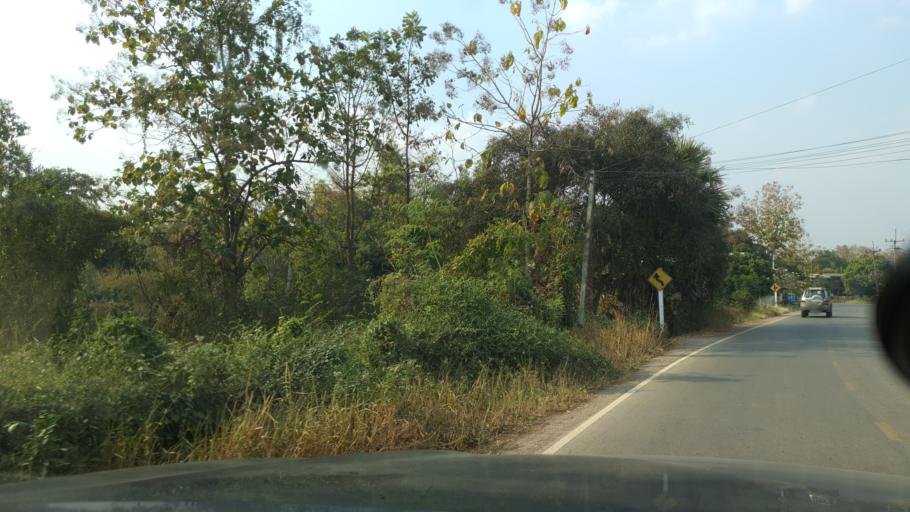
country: TH
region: Sukhothai
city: Ban Dan Lan Hoi
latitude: 17.1150
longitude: 99.5390
